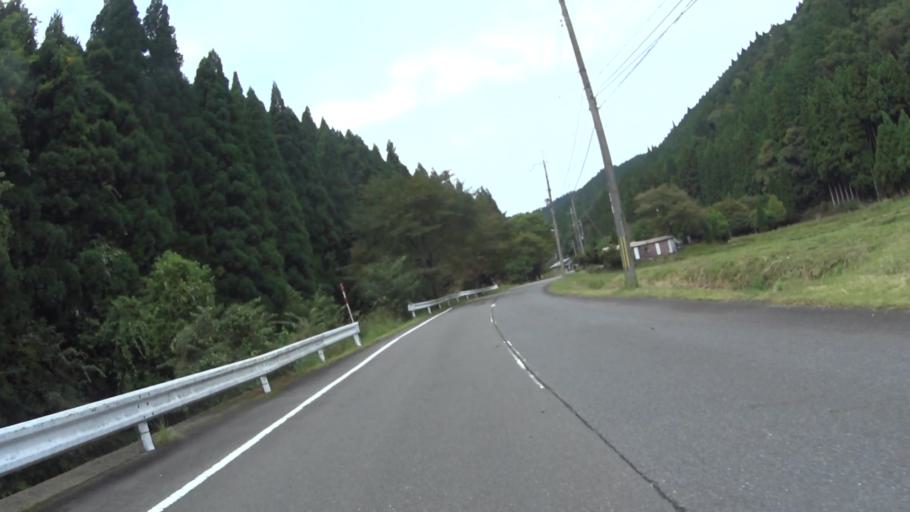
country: JP
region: Shiga Prefecture
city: Kitahama
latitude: 35.2633
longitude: 135.7472
